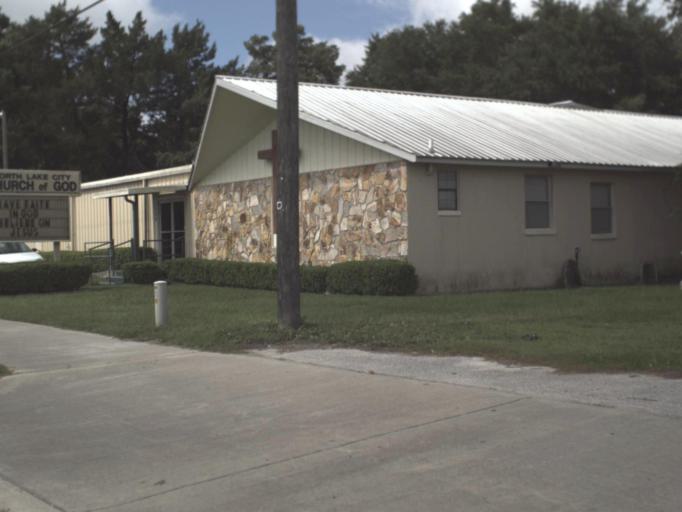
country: US
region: Florida
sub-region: Columbia County
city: Five Points
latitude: 30.2136
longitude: -82.6379
